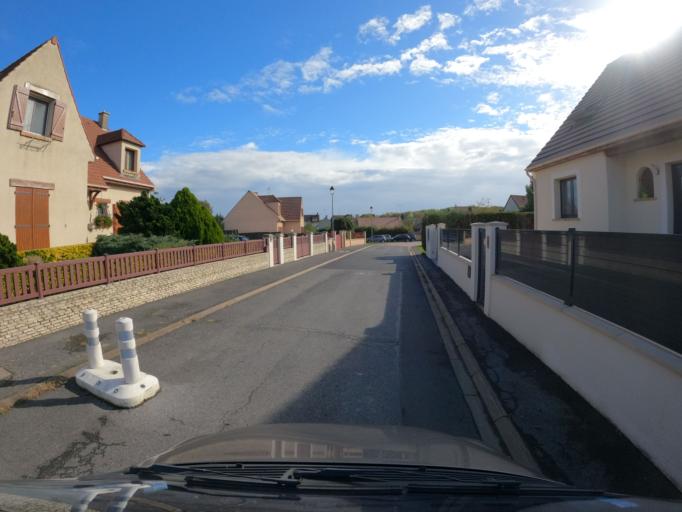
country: FR
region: Ile-de-France
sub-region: Departement de Seine-et-Marne
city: Saint-Germain-sur-Morin
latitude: 48.8804
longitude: 2.8491
